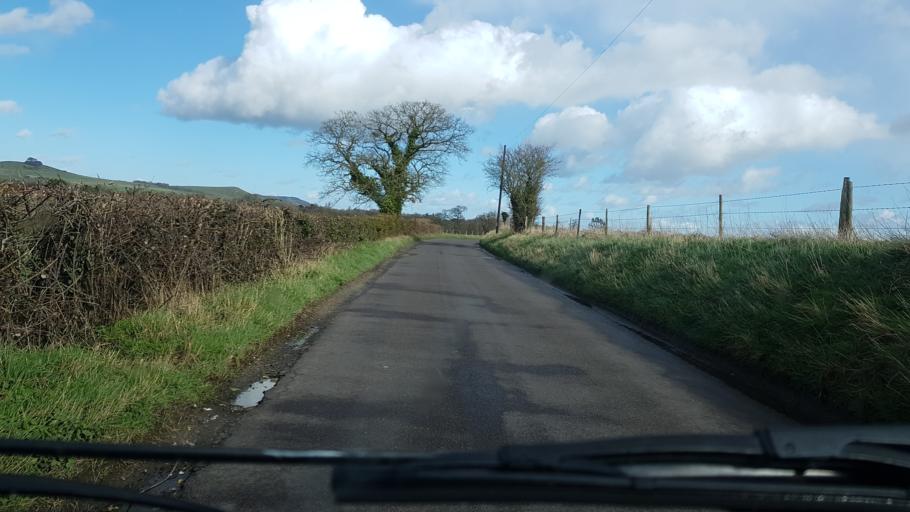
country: GB
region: England
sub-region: Wiltshire
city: Woodborough
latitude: 51.3334
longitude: -1.8578
